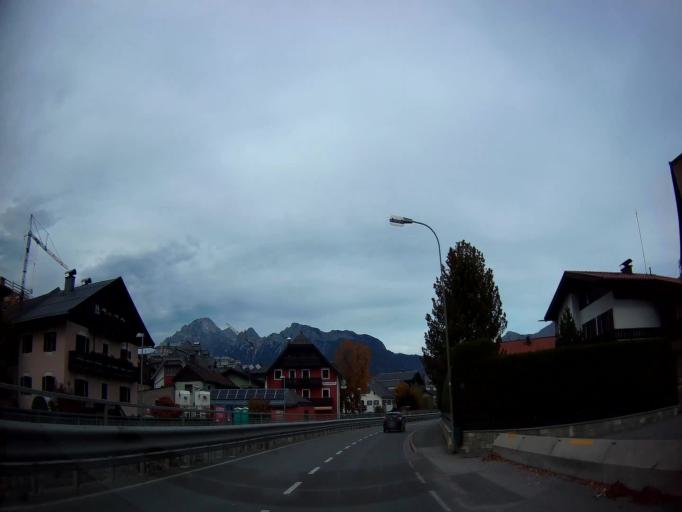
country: AT
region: Salzburg
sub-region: Politischer Bezirk Zell am See
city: Saalfelden am Steinernen Meer
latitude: 47.4239
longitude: 12.8486
